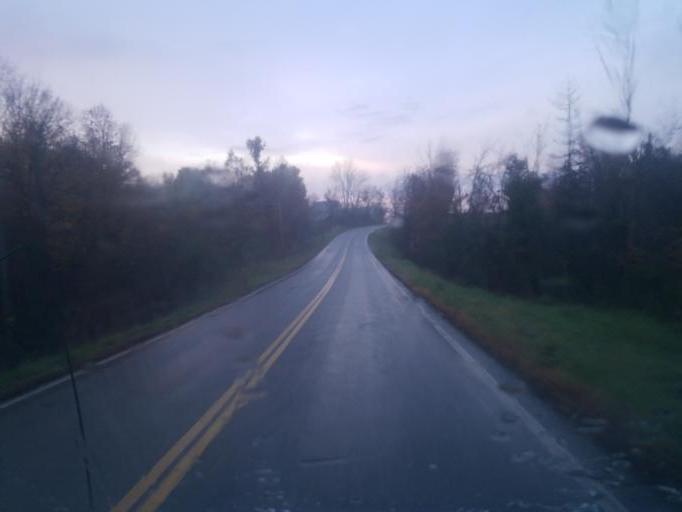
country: US
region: Ohio
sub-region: Morgan County
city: McConnelsville
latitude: 39.5149
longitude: -81.8507
